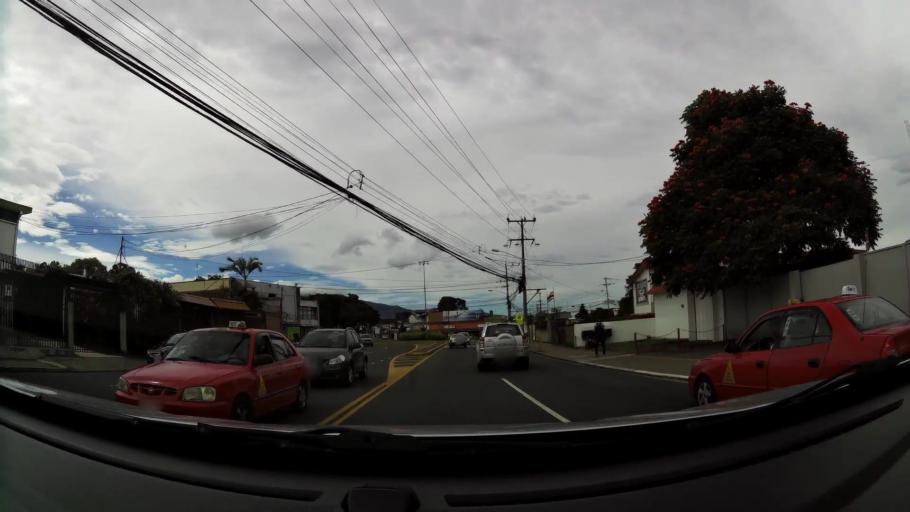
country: CR
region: San Jose
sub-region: Canton de Goicoechea
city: Guadalupe
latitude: 9.9397
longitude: -84.0524
